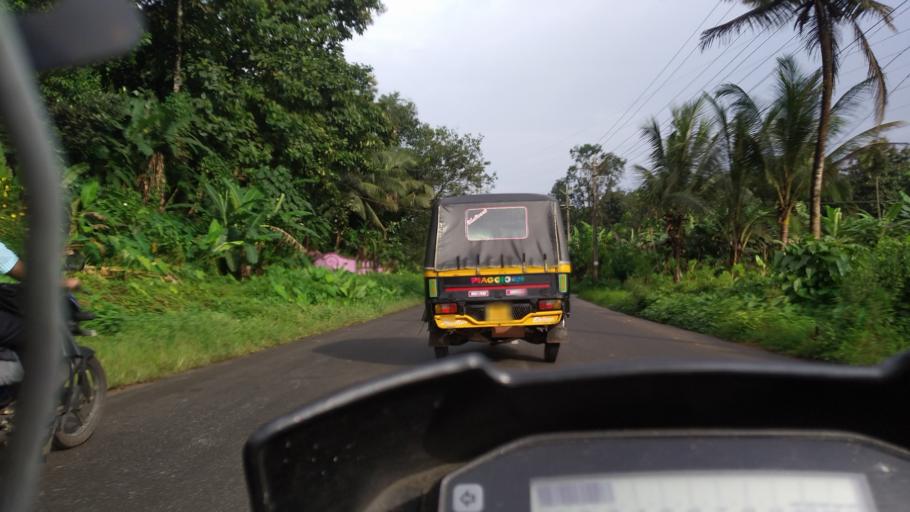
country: IN
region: Kerala
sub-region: Ernakulam
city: Kotamangalam
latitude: 10.0530
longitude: 76.7023
